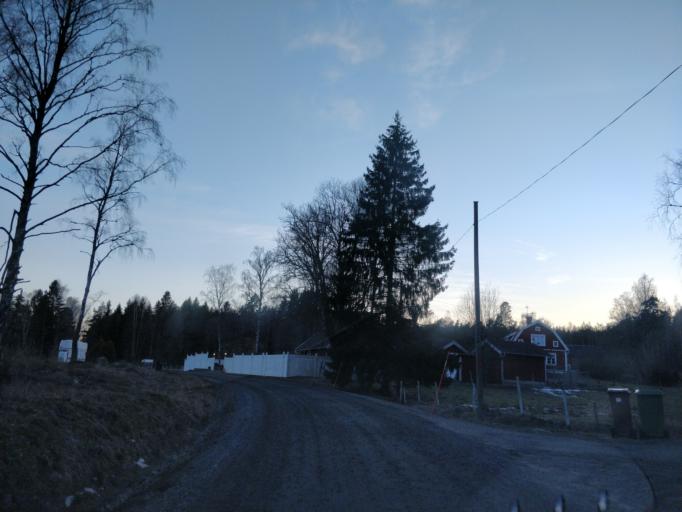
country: SE
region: Uppsala
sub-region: Enkopings Kommun
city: Orsundsbro
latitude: 59.8268
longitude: 17.1591
